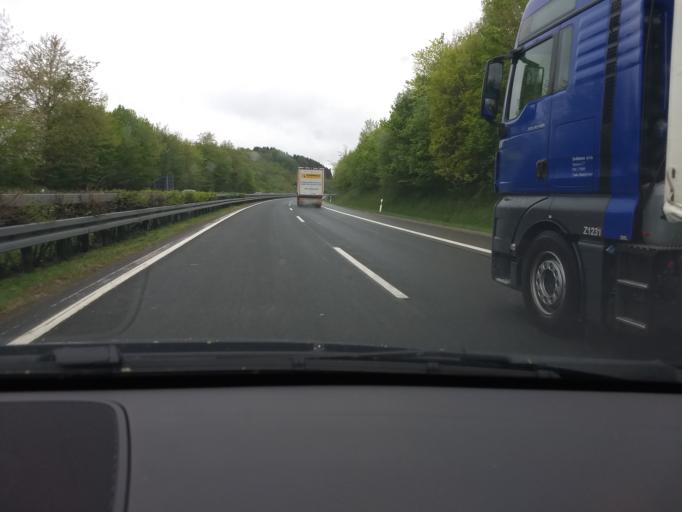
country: DE
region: North Rhine-Westphalia
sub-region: Regierungsbezirk Arnsberg
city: Meschede
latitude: 51.3587
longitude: 8.3356
